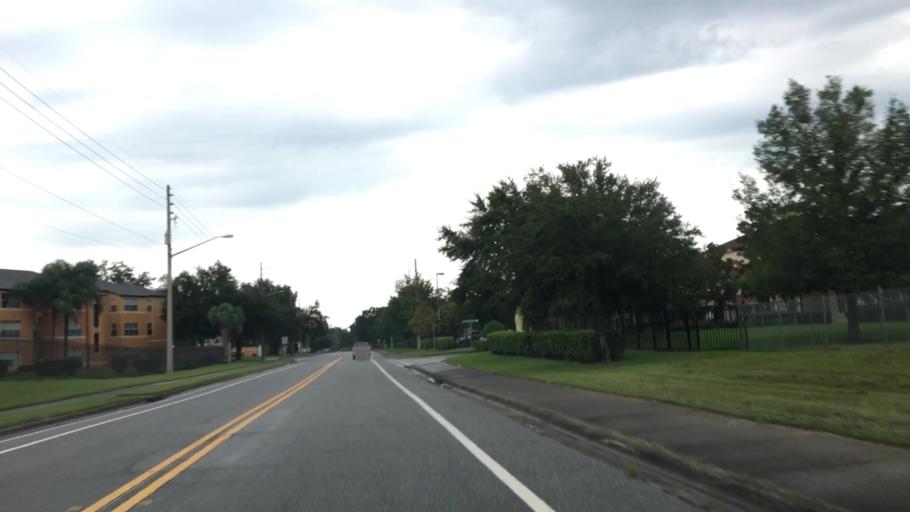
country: US
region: Florida
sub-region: Orange County
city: Conway
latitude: 28.4966
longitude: -81.3062
